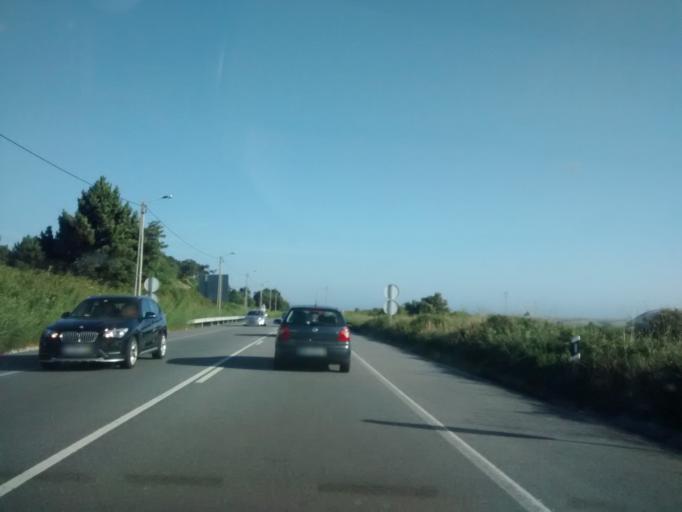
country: PT
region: Viana do Castelo
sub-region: Viana do Castelo
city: Areosa
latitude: 41.7401
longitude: -8.8638
